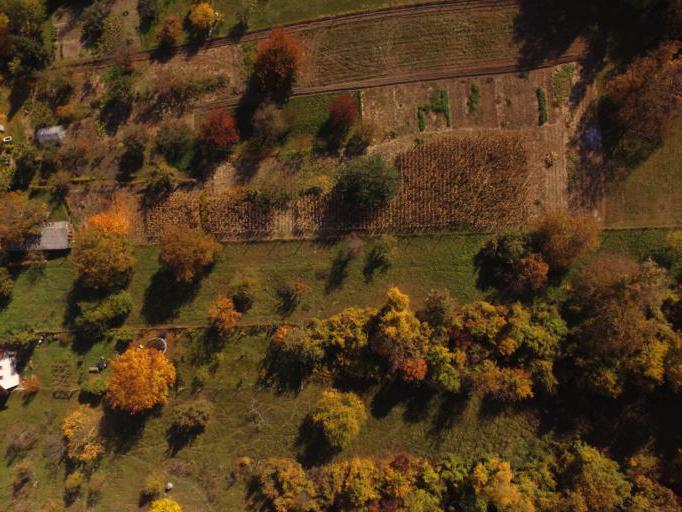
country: HU
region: Fejer
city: Bicske
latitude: 47.5187
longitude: 18.6102
